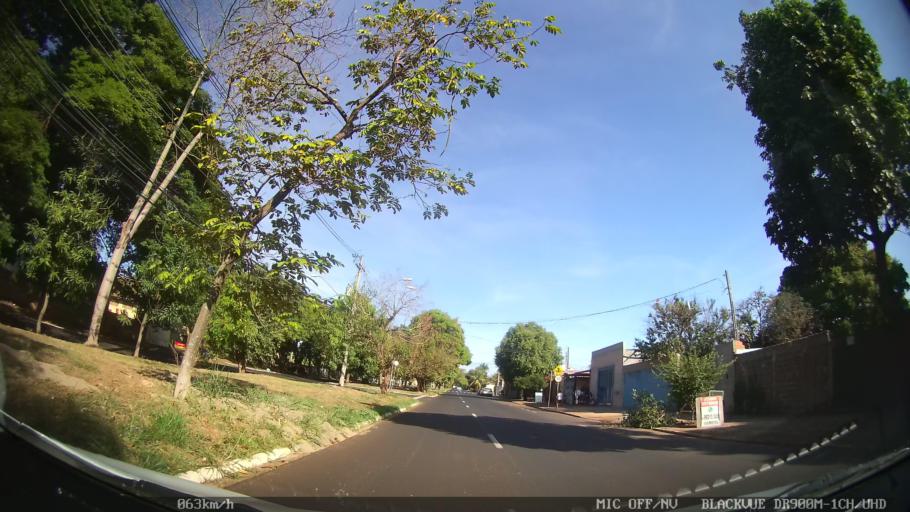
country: BR
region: Sao Paulo
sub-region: Ribeirao Preto
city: Ribeirao Preto
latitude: -21.1868
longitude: -47.7611
